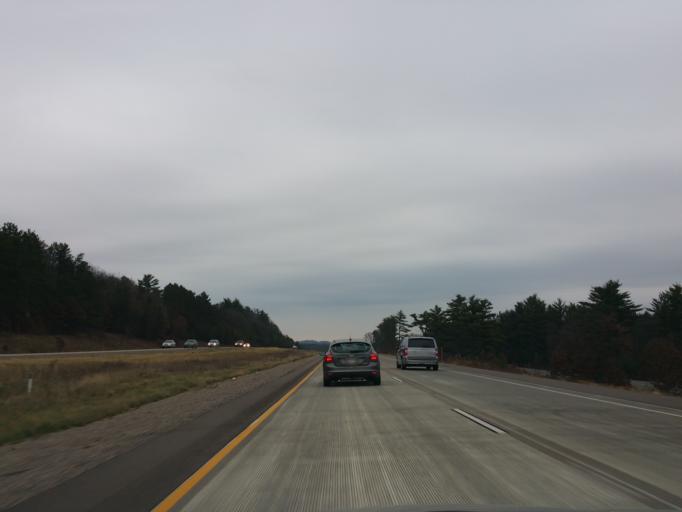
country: US
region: Wisconsin
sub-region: Jackson County
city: Black River Falls
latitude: 44.3275
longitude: -90.8893
